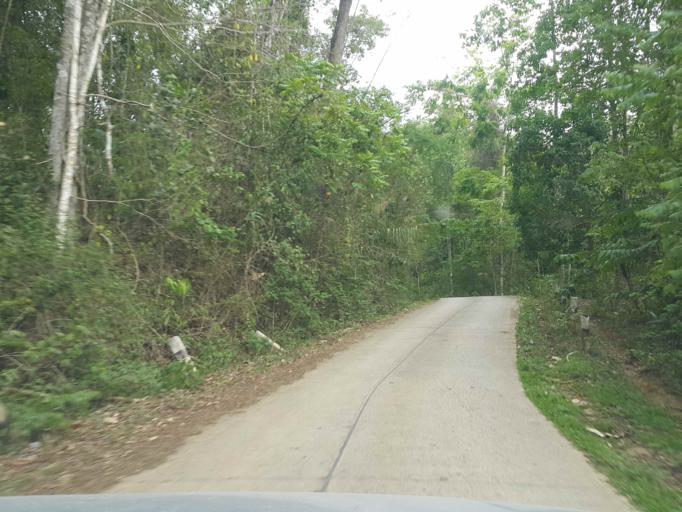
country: TH
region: Chiang Mai
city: Wiang Haeng
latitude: 19.3764
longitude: 98.7512
